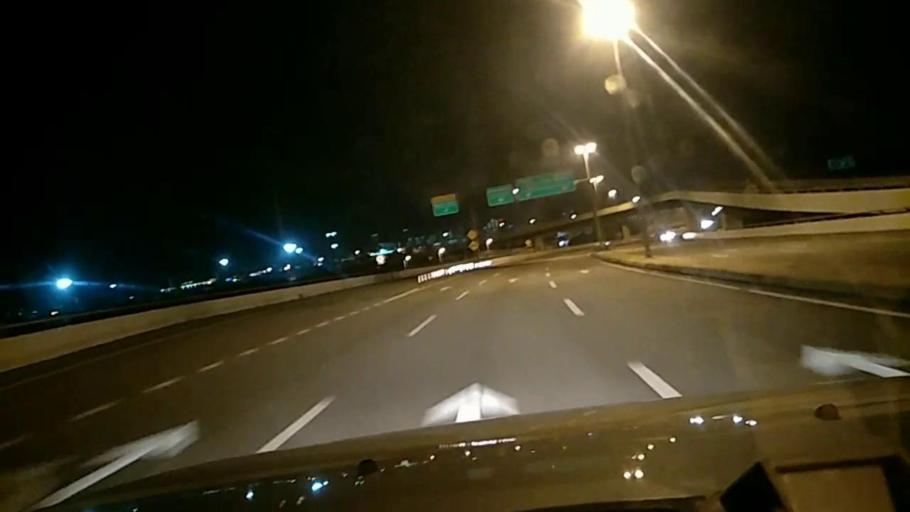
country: MY
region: Penang
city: Butterworth
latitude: 5.3909
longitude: 100.3719
